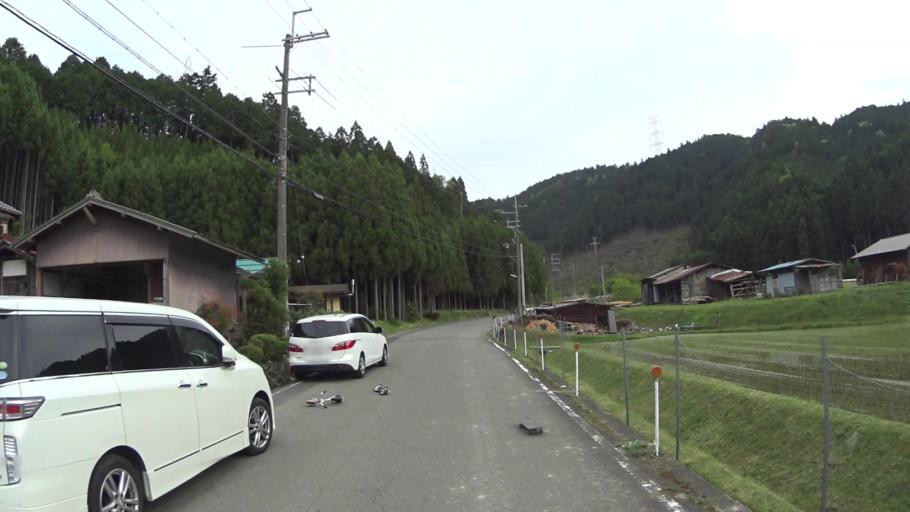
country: JP
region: Kyoto
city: Kameoka
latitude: 35.1266
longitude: 135.6288
